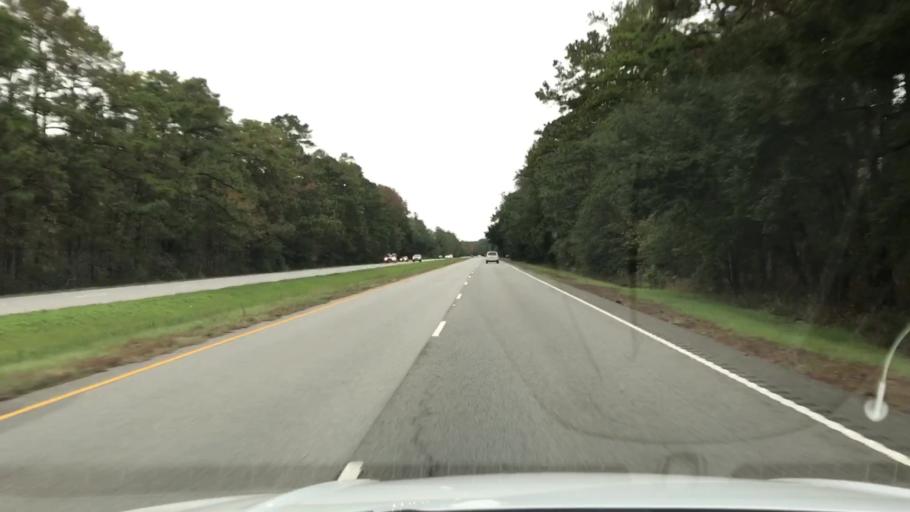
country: US
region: South Carolina
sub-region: Georgetown County
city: Georgetown
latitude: 33.3954
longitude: -79.2021
